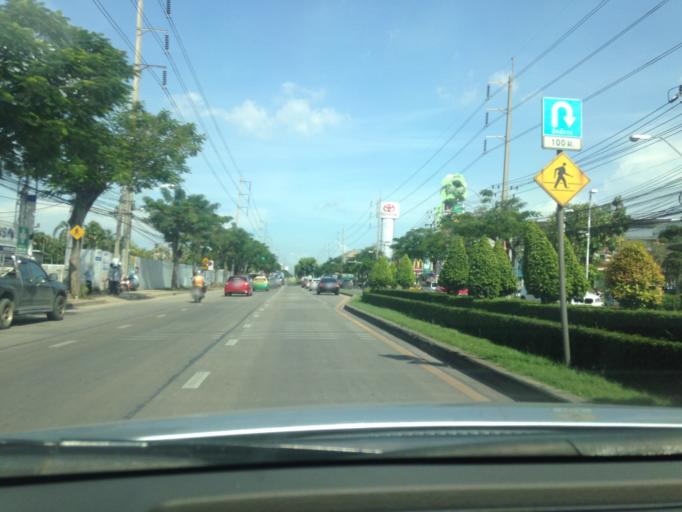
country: TH
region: Bangkok
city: Lat Krabang
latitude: 13.7222
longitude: 100.7265
